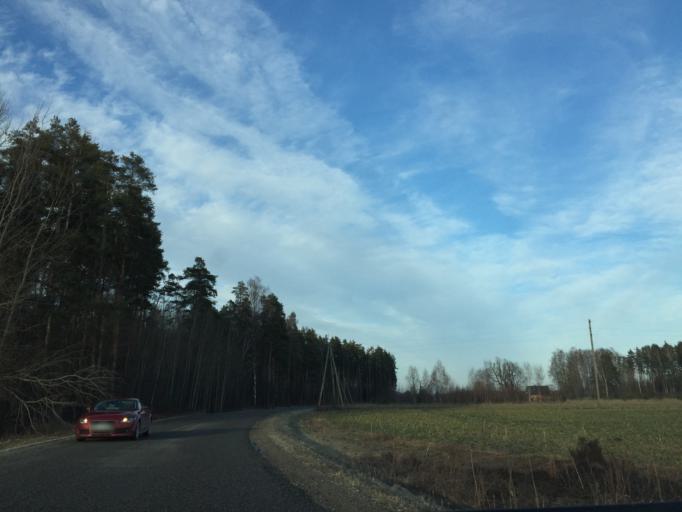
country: LV
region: Kekava
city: Kekava
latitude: 56.8185
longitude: 24.1846
